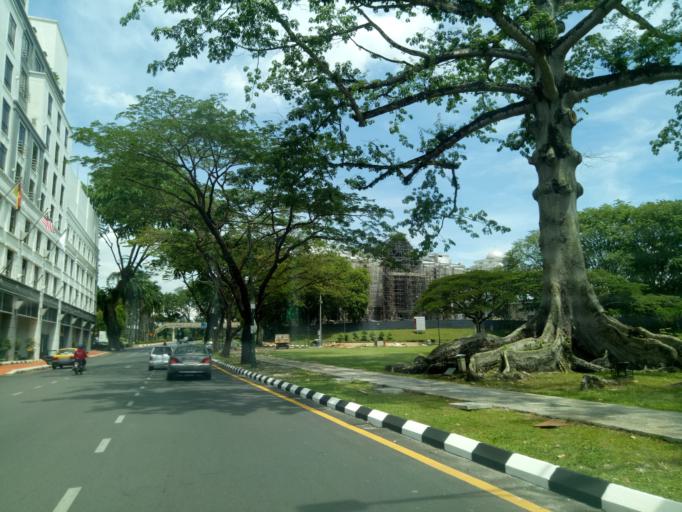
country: MY
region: Sarawak
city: Kuching
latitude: 1.5567
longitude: 110.3440
